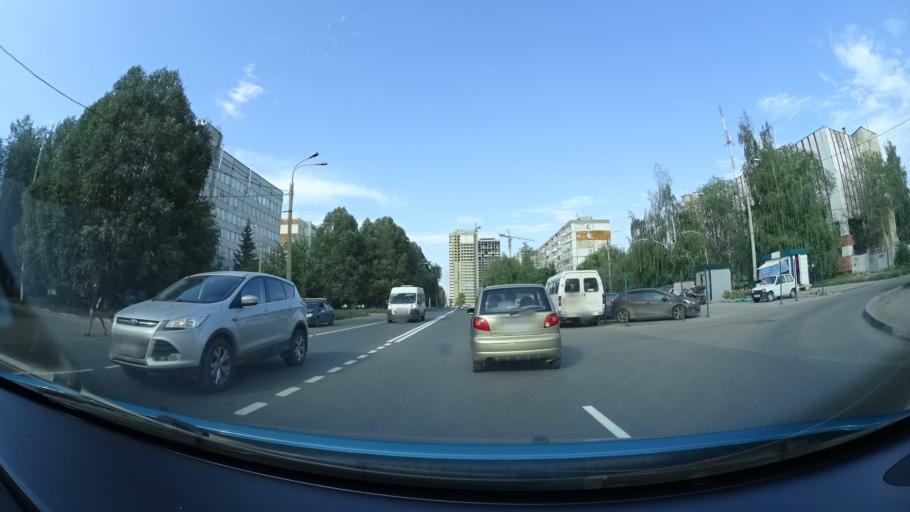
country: RU
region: Samara
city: Samara
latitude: 53.2635
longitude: 50.2269
